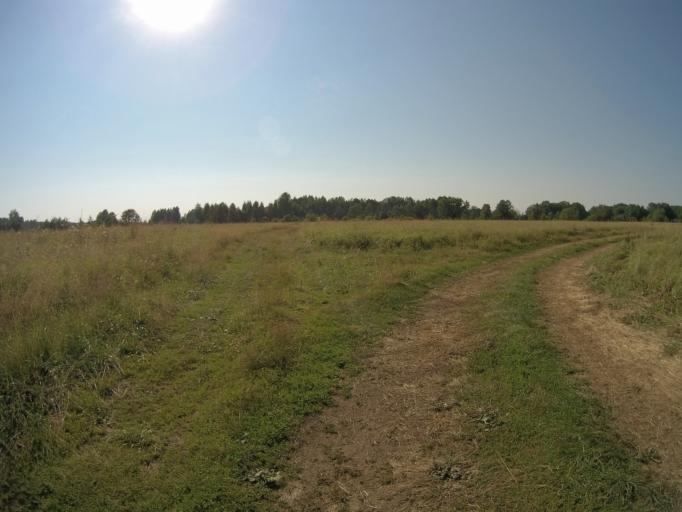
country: RU
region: Vladimir
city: Vorsha
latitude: 56.0268
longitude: 40.1981
